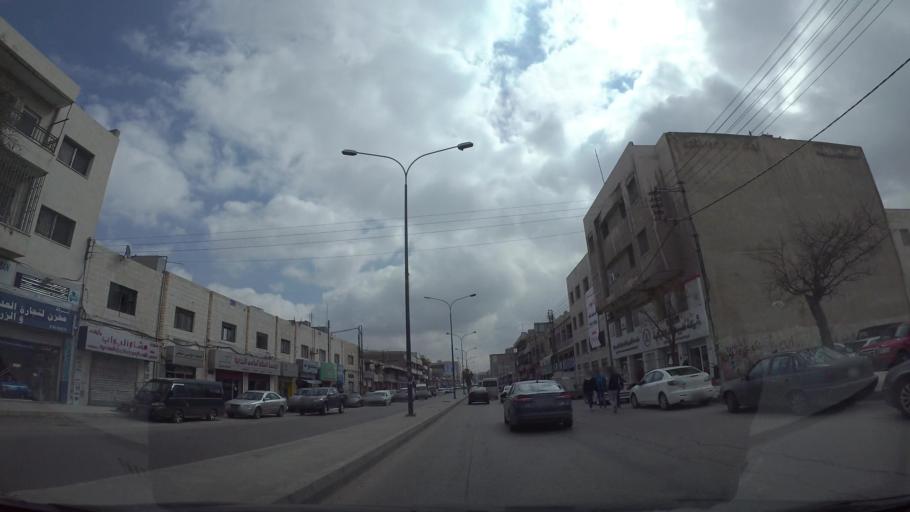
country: JO
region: Amman
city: Al Quwaysimah
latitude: 31.9238
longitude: 35.9380
